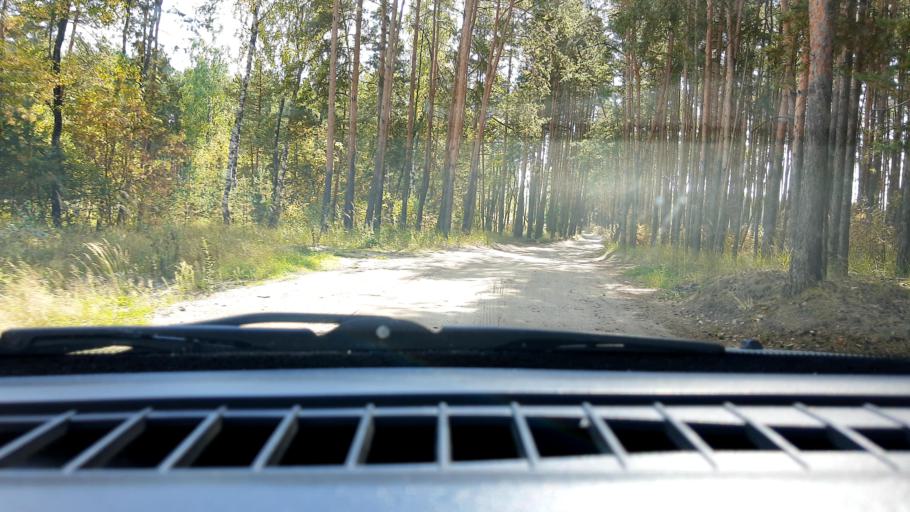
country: RU
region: Nizjnij Novgorod
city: Gorbatovka
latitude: 56.3093
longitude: 43.6996
